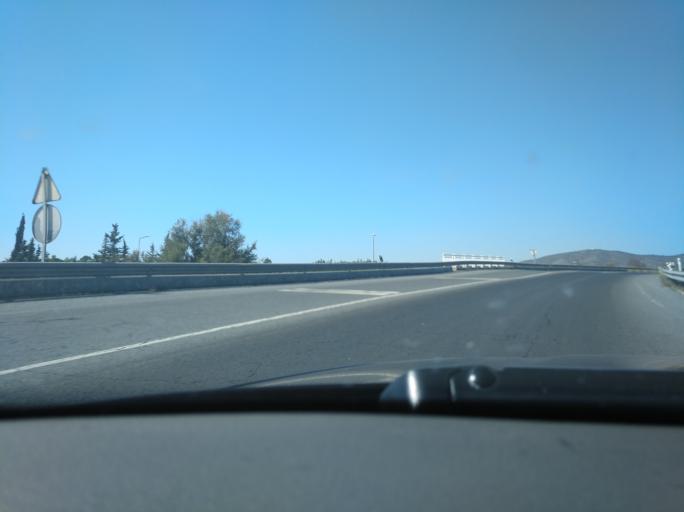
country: PT
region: Faro
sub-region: Olhao
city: Olhao
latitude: 37.0447
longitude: -7.8193
